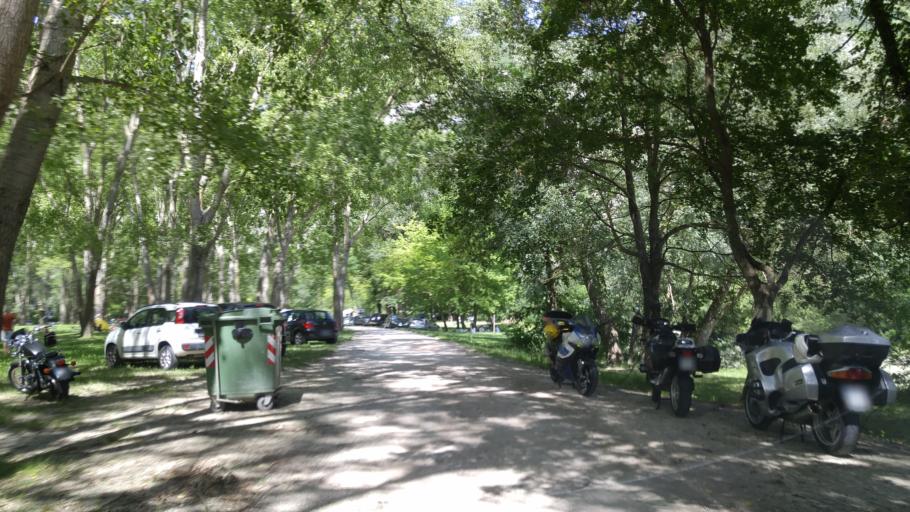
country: IT
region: The Marches
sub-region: Provincia di Pesaro e Urbino
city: Acqualagna
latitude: 43.6385
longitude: 12.7148
